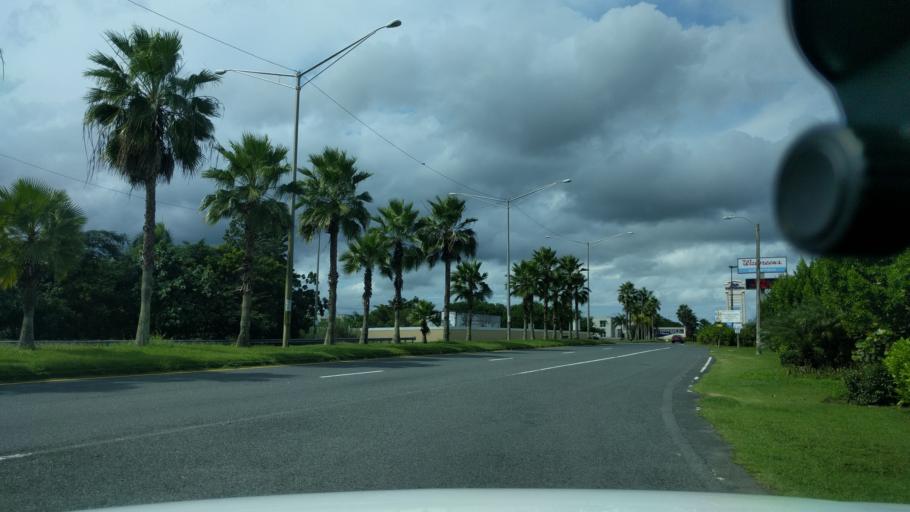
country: PR
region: Toa Alta
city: Pajaros
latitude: 18.3399
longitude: -66.2031
